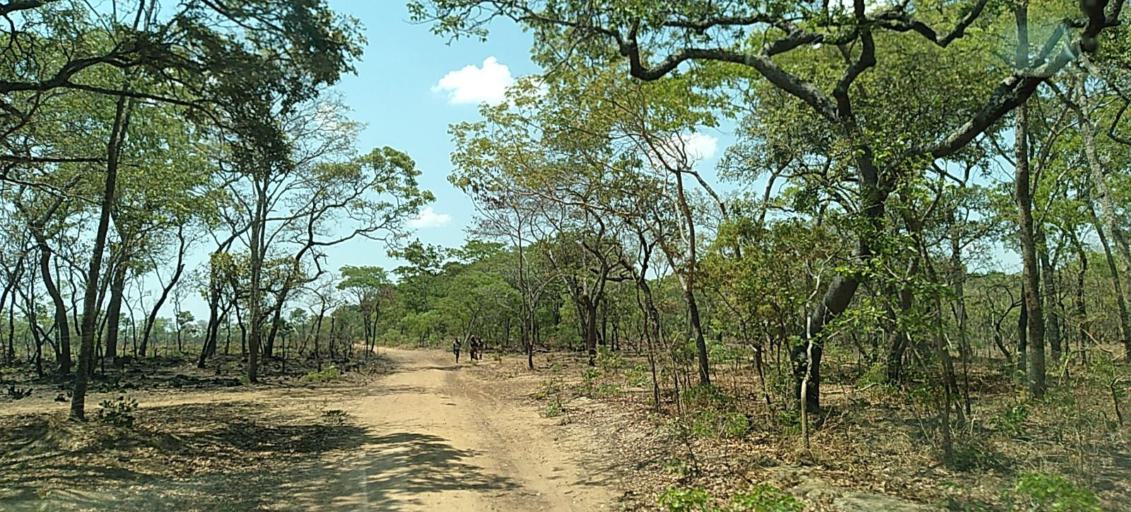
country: ZM
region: Copperbelt
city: Mpongwe
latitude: -13.6532
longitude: 28.4879
